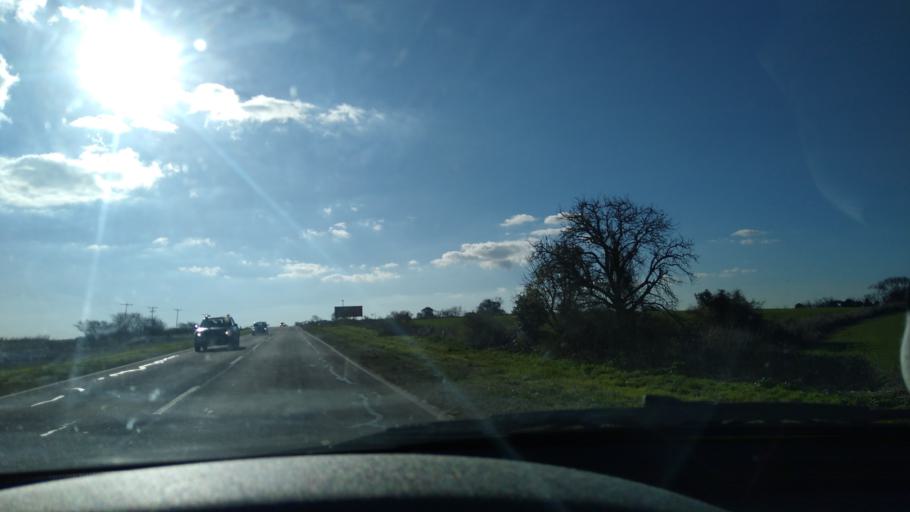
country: AR
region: Entre Rios
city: Diamante
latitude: -32.1098
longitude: -60.5777
